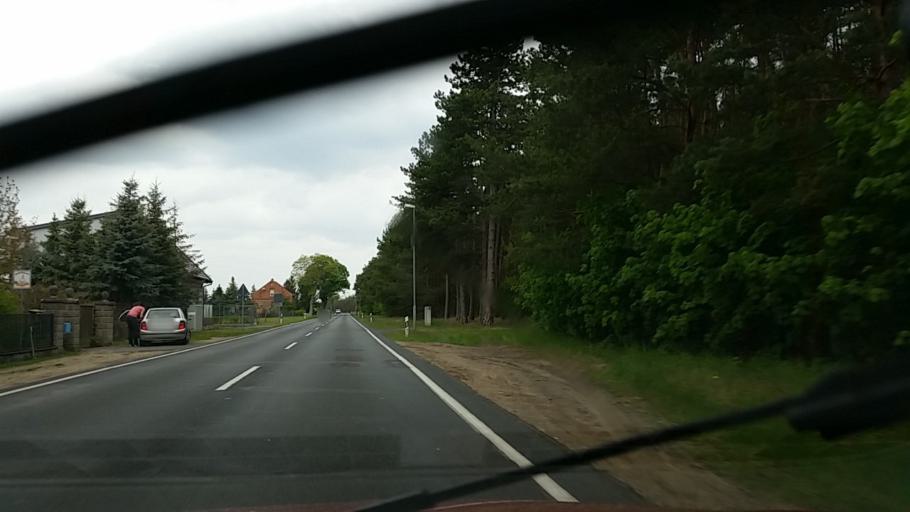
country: DE
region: Brandenburg
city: Spreenhagen
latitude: 52.3299
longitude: 13.8982
